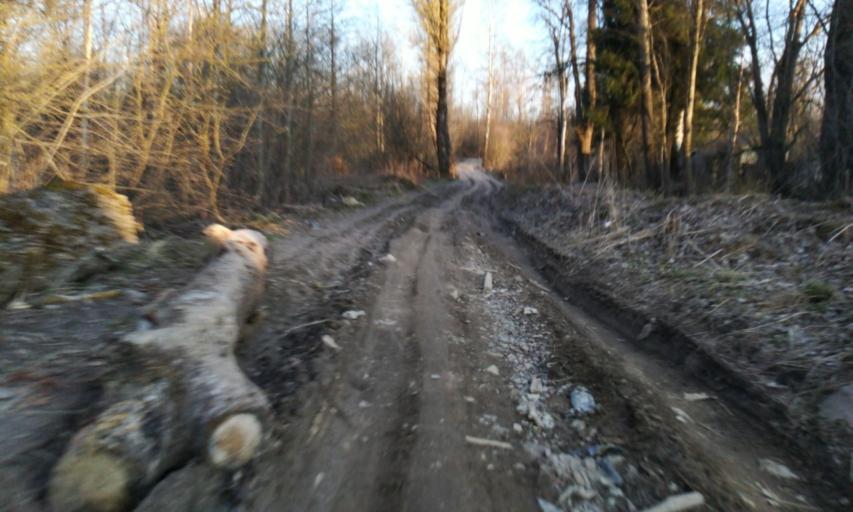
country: RU
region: Leningrad
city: Novoye Devyatkino
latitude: 60.0854
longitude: 30.4588
